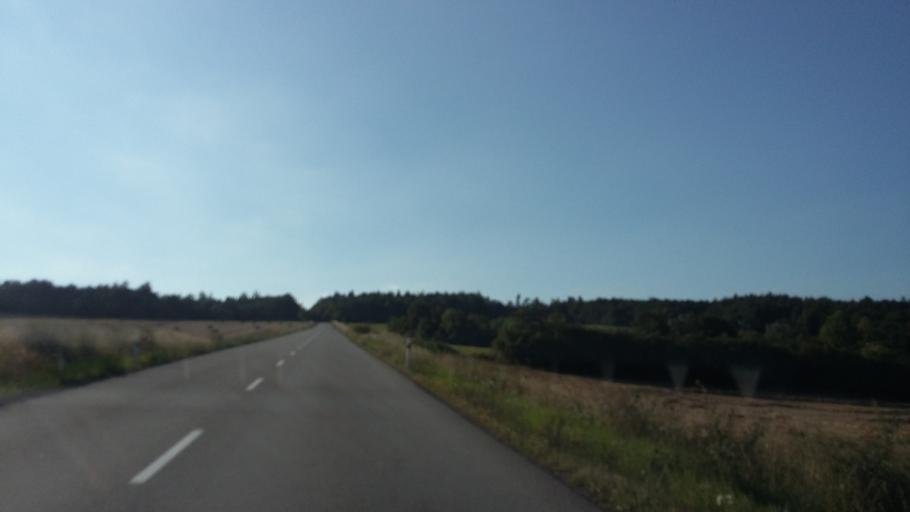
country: CZ
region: South Moravian
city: Ricany
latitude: 49.2169
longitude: 16.3807
